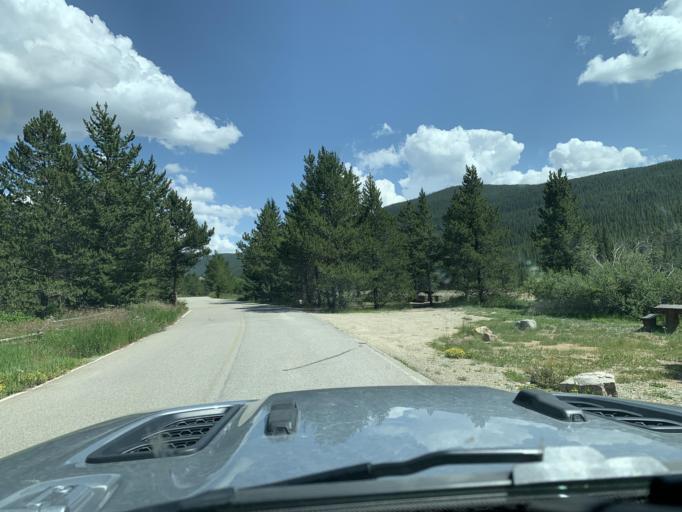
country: US
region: Colorado
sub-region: Lake County
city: Leadville North
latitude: 39.2782
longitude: -106.4337
